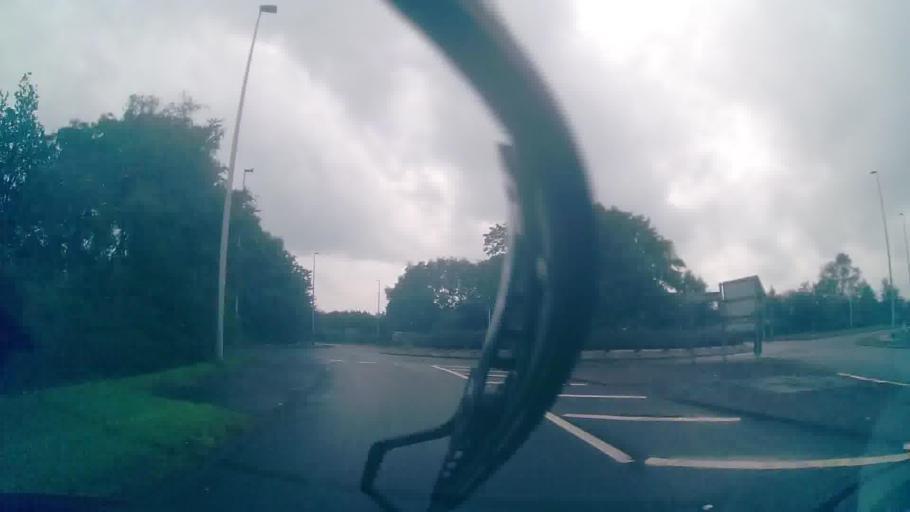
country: GB
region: Scotland
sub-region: Dumfries and Galloway
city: Locharbriggs
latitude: 55.0696
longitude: -3.5568
